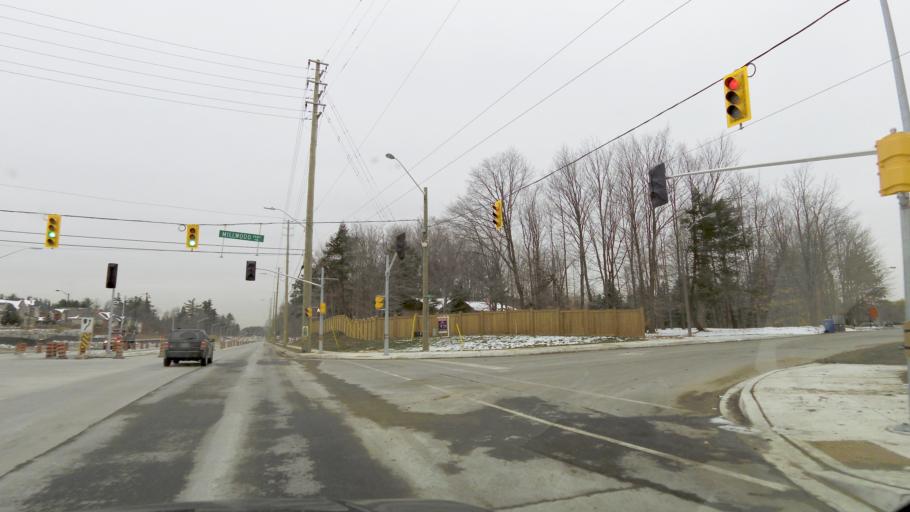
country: CA
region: Ontario
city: Vaughan
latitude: 43.8419
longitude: -79.5763
